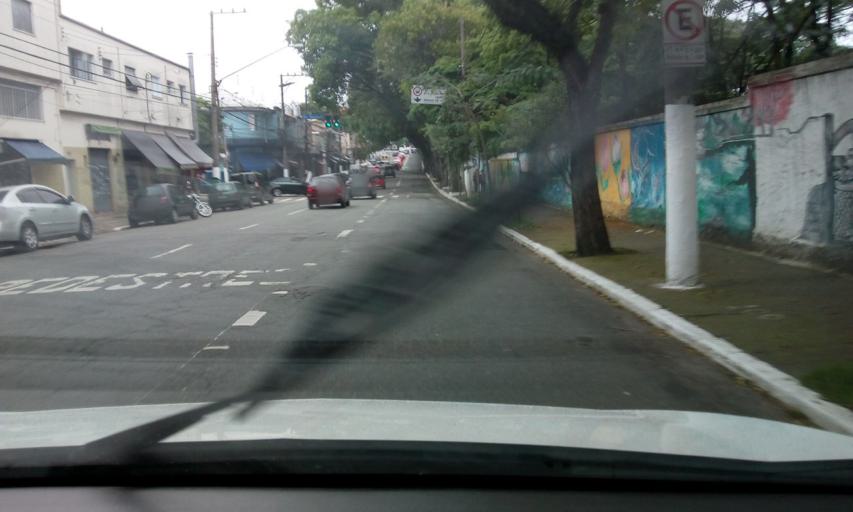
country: BR
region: Sao Paulo
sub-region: Sao Paulo
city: Sao Paulo
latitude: -23.5791
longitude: -46.6258
